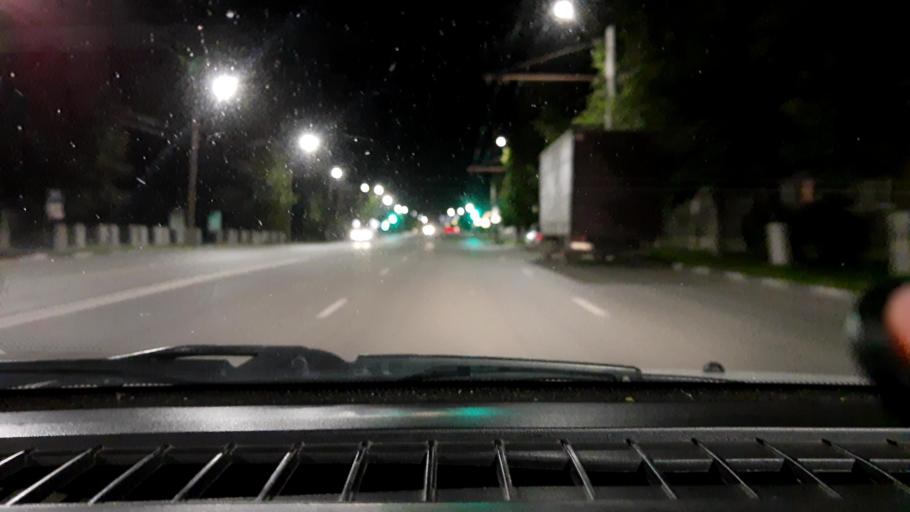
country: RU
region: Nizjnij Novgorod
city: Dzerzhinsk
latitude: 56.2409
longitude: 43.4823
